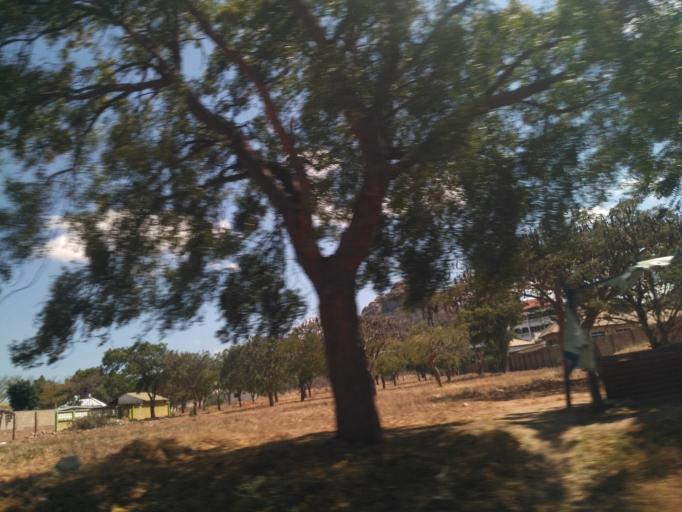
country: TZ
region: Dodoma
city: Dodoma
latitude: -6.1616
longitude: 35.7590
